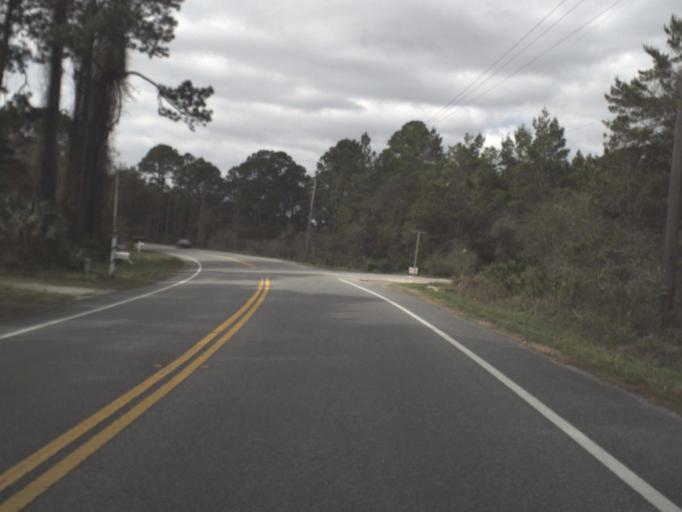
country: US
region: Florida
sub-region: Franklin County
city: Carrabelle
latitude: 29.8251
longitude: -84.7046
